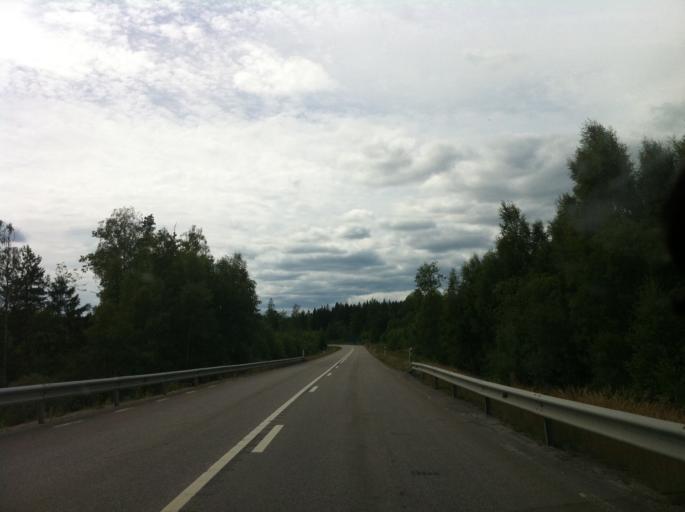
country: SE
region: Kronoberg
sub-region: Tingsryds Kommun
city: Tingsryd
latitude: 56.5069
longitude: 15.1415
